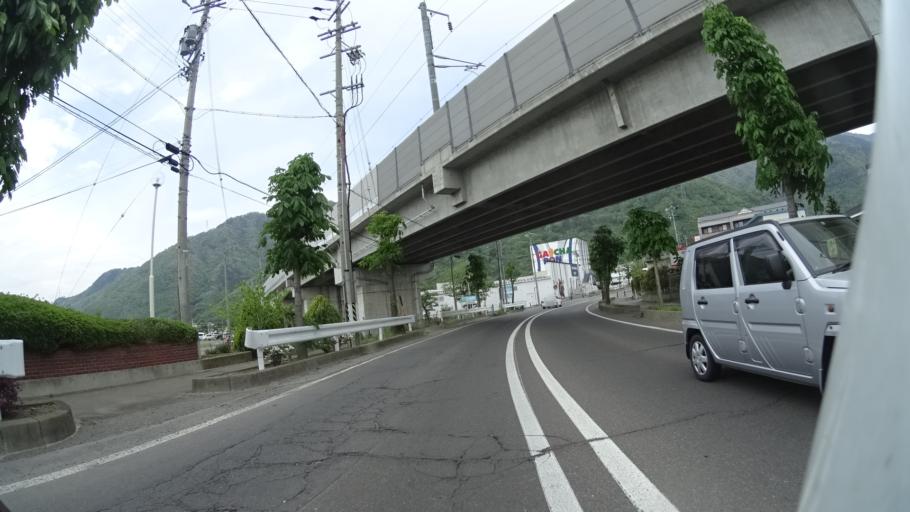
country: JP
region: Nagano
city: Ueda
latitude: 36.4130
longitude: 138.2243
